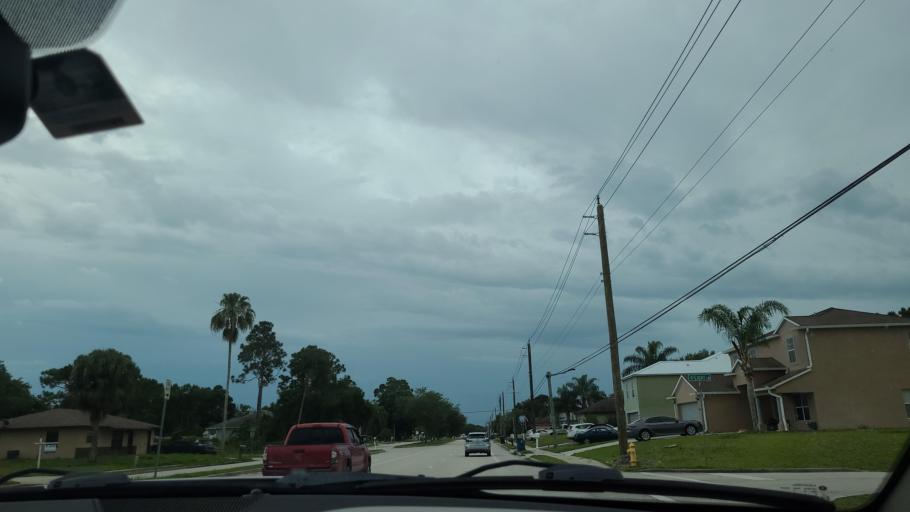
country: US
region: Florida
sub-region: Brevard County
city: Grant-Valkaria
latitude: 27.9634
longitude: -80.6487
